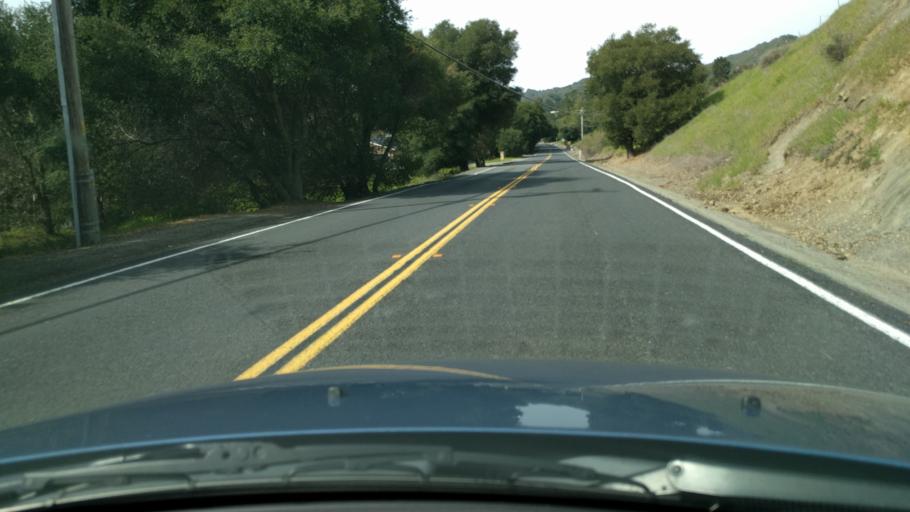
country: US
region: California
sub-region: Contra Costa County
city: Danville
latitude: 37.8033
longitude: -122.0334
